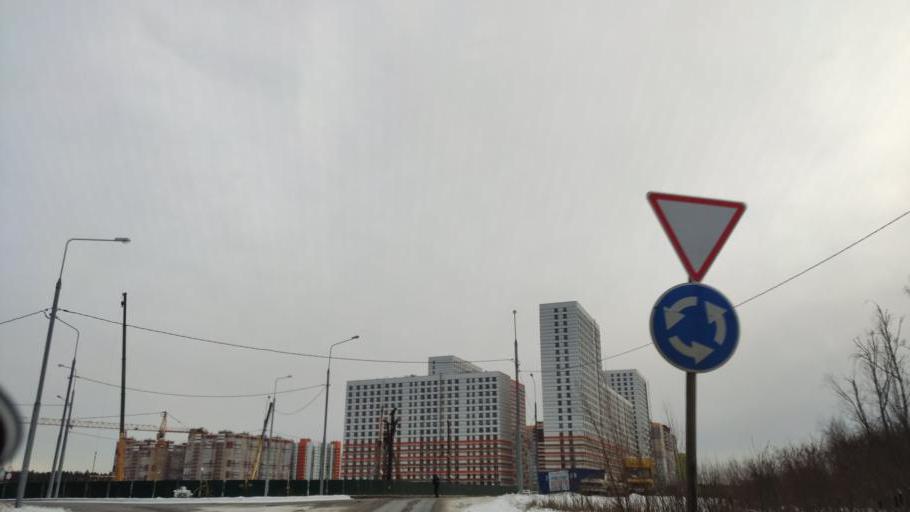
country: RU
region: Moscow
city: Annino
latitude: 55.5396
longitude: 37.6132
